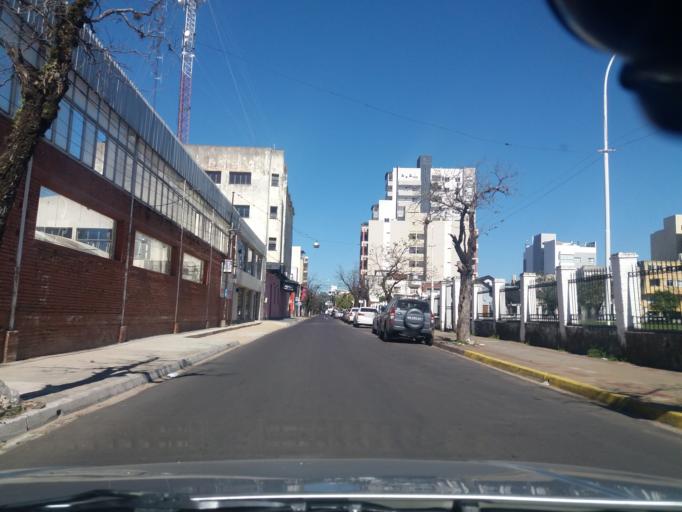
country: AR
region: Corrientes
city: Corrientes
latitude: -27.4722
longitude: -58.8395
